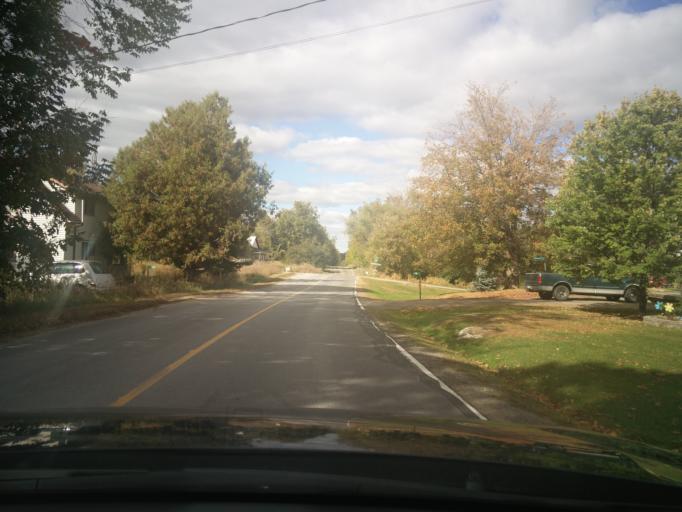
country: CA
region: Ontario
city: Perth
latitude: 44.6570
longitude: -76.5418
